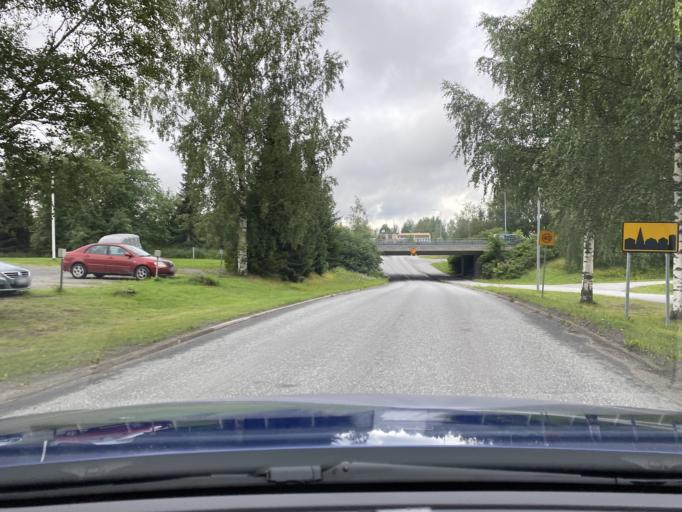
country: FI
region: Ostrobothnia
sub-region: Kyroenmaa
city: Laihia
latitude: 62.9796
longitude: 22.0120
